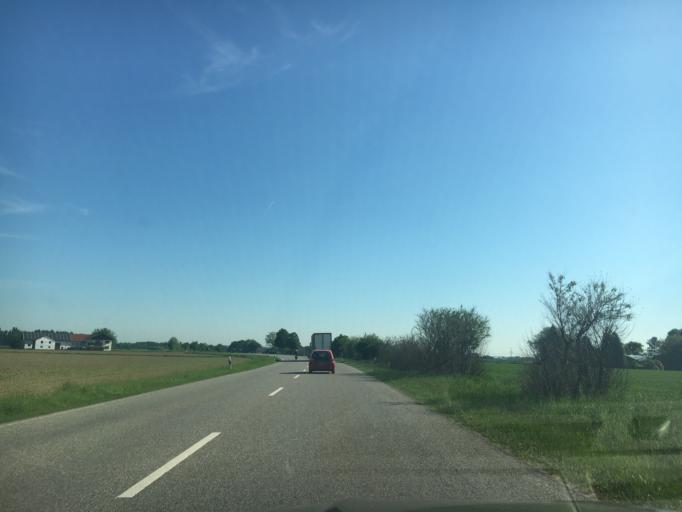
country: DE
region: Bavaria
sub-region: Upper Bavaria
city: Unterneukirchen
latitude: 48.1916
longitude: 12.6408
